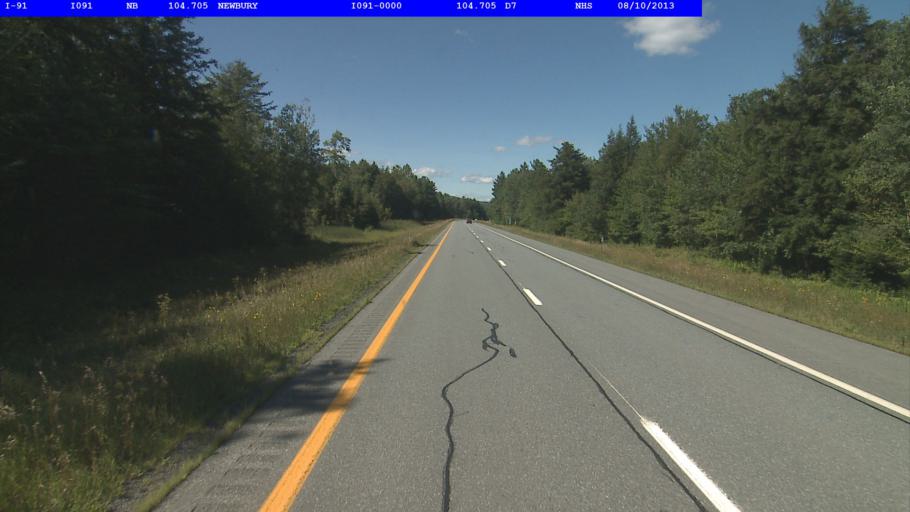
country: US
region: New Hampshire
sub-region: Grafton County
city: Haverhill
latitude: 44.0811
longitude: -72.1120
